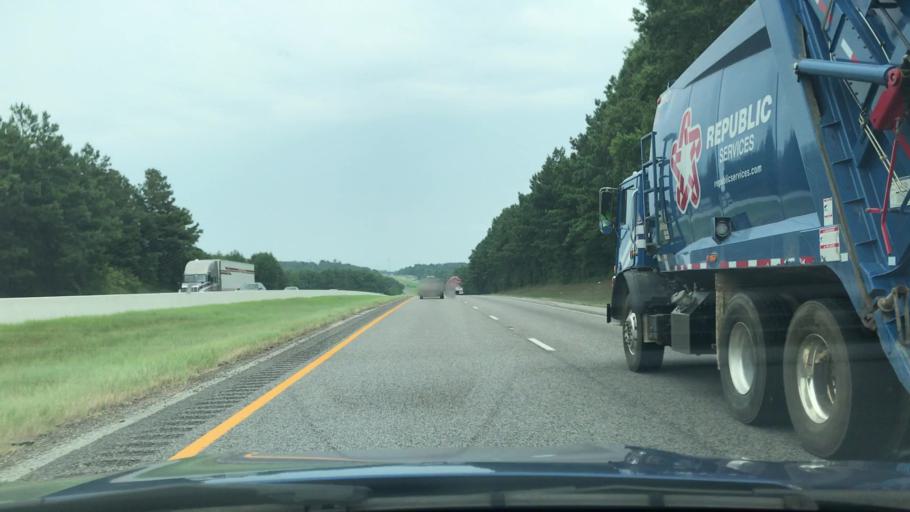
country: US
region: Texas
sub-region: Smith County
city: Lindale
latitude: 32.4599
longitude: -95.3170
